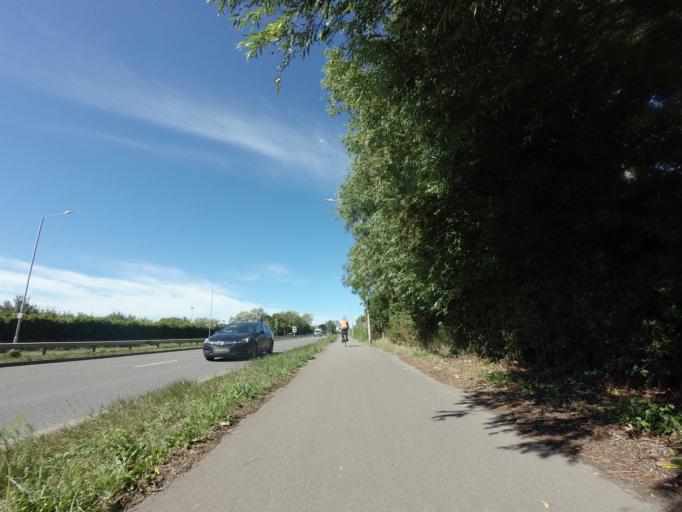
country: GB
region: England
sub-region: Kent
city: Sandwich
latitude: 51.2975
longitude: 1.3471
